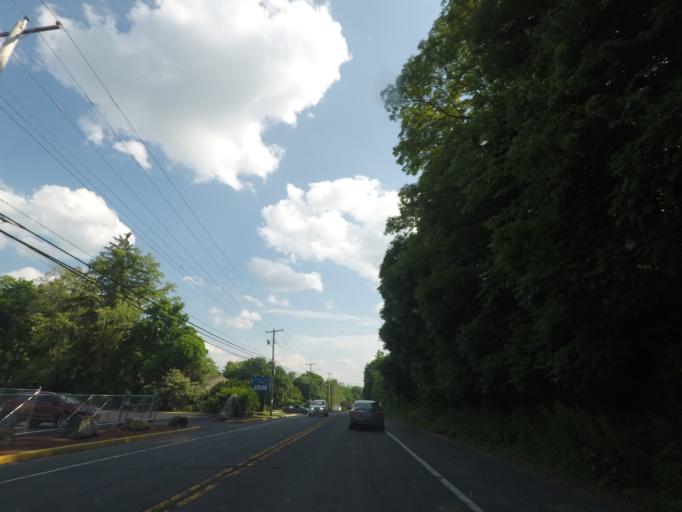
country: US
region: New York
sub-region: Orange County
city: Balmville
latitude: 41.5404
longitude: -74.0128
